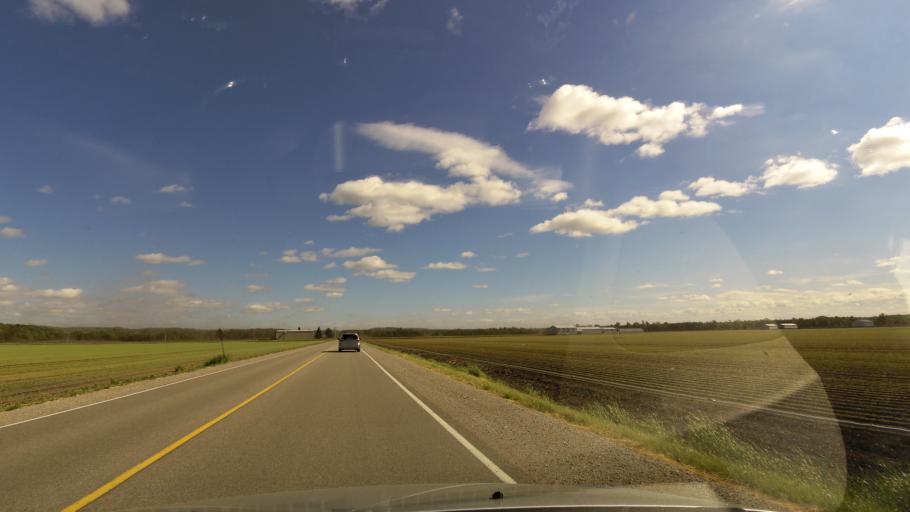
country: CA
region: Ontario
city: Innisfil
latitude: 44.2232
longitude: -79.6324
